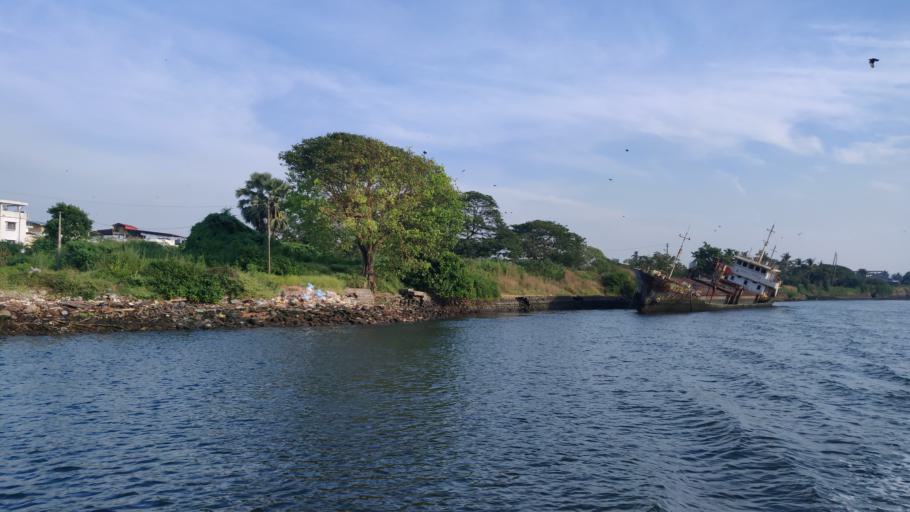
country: IN
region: Karnataka
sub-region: Dakshina Kannada
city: Mangalore
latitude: 12.8727
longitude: 74.8289
